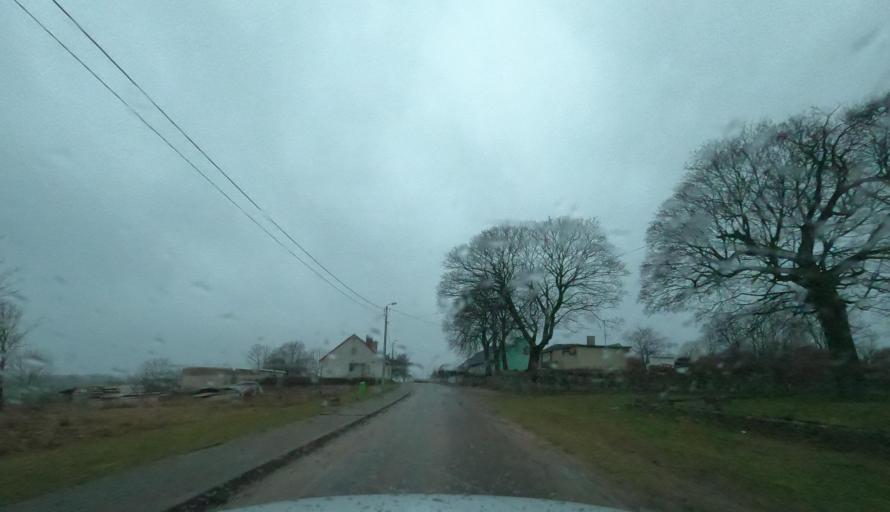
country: PL
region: West Pomeranian Voivodeship
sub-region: Powiat szczecinecki
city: Borne Sulinowo
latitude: 53.7084
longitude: 16.5342
